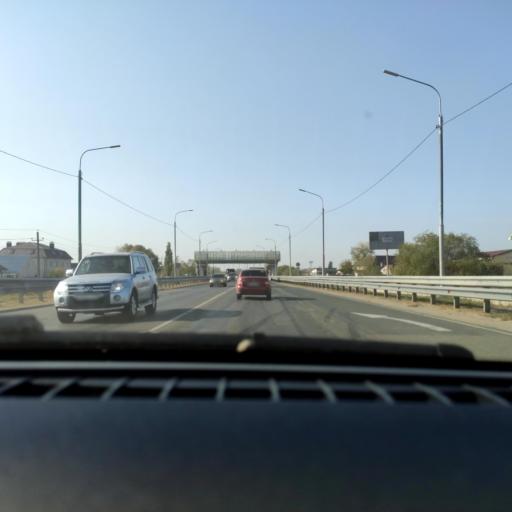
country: RU
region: Voronezj
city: Somovo
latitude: 51.6906
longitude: 39.3652
